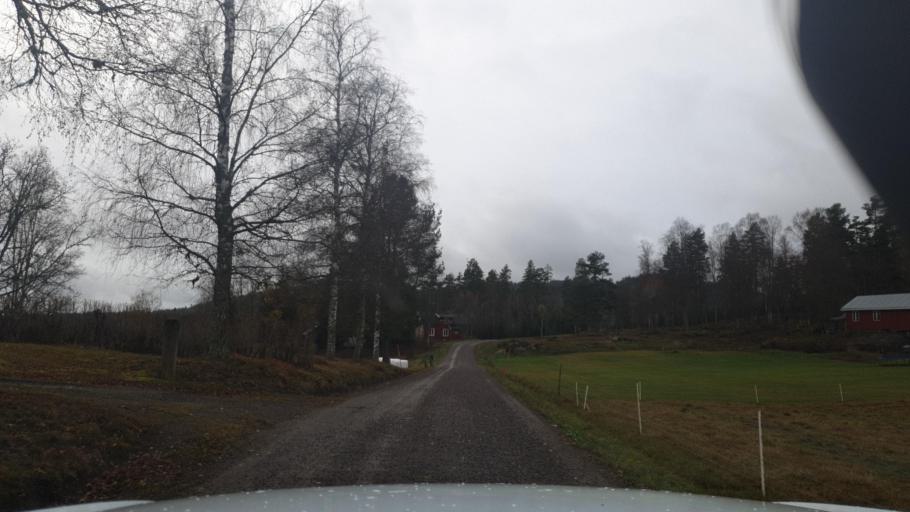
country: NO
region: Ostfold
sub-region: Romskog
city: Romskog
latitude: 59.8160
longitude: 11.9965
